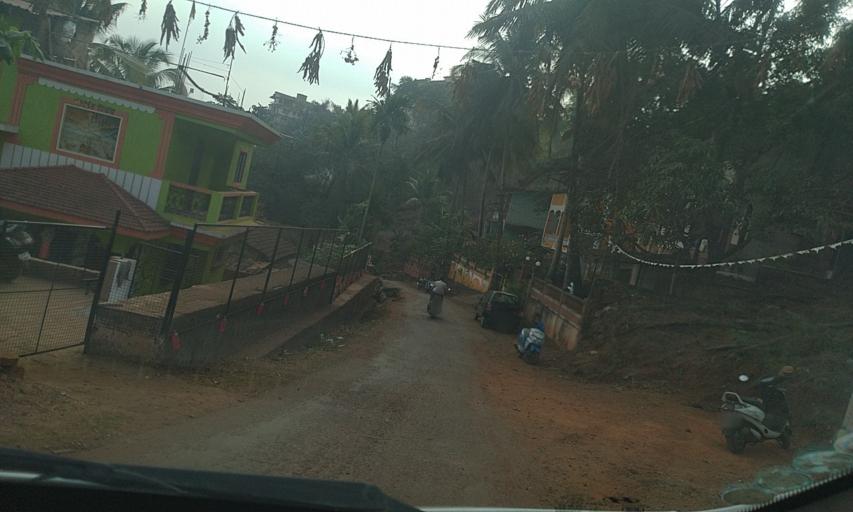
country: IN
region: Goa
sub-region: North Goa
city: Taleigao
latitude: 15.4636
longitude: 73.8161
